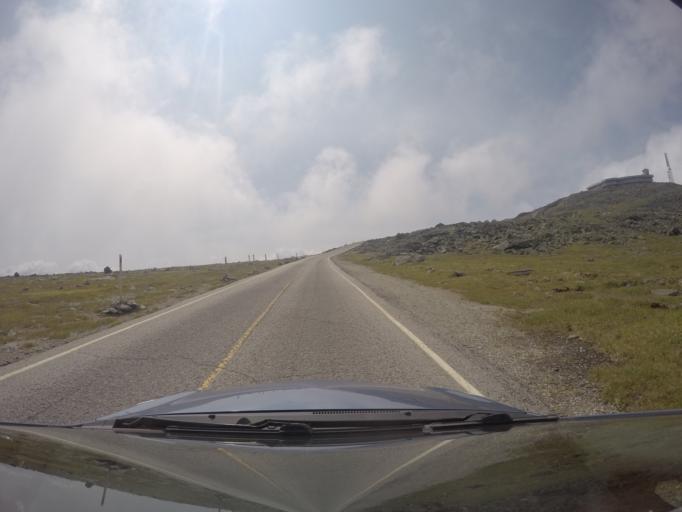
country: US
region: New Hampshire
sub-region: Coos County
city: Gorham
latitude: 44.2734
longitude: -71.3015
